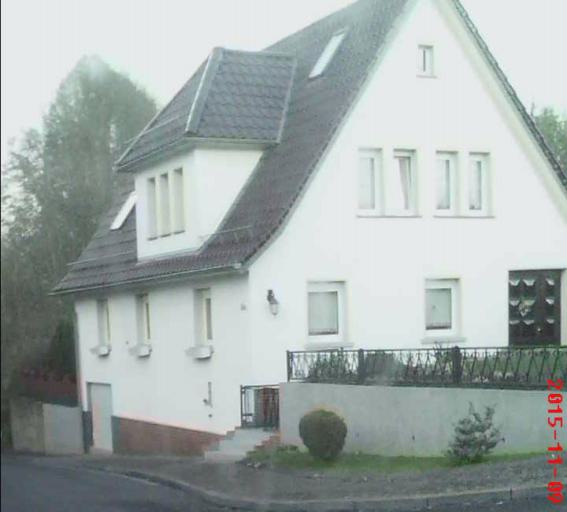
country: DE
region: Thuringia
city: Pfaffschwende
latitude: 51.2498
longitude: 10.0961
